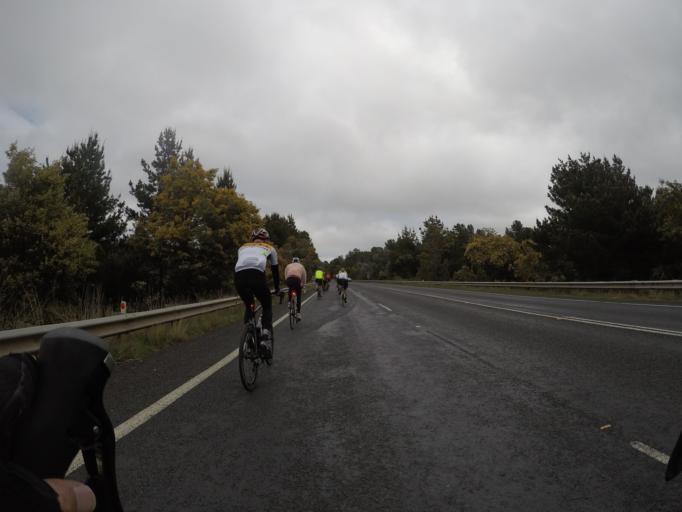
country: AU
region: New South Wales
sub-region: Lithgow
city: Portland
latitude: -33.4381
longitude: 149.8454
